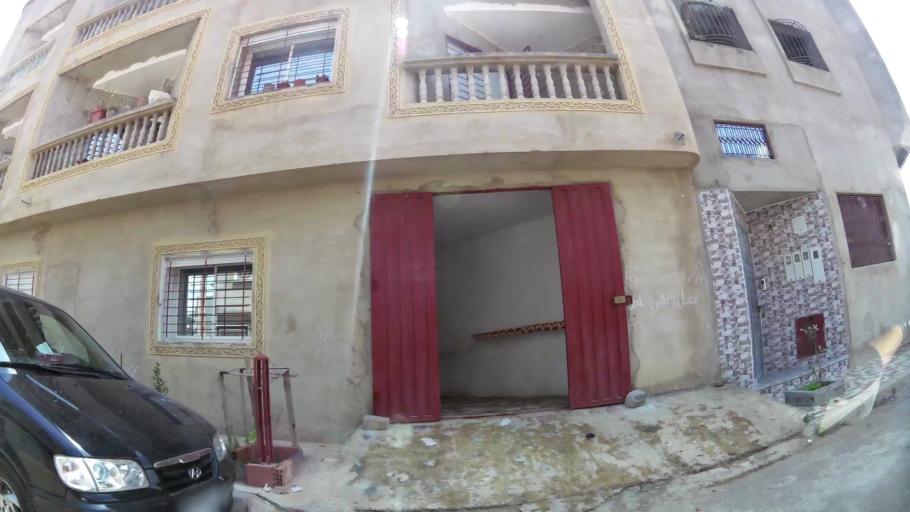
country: MA
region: Rabat-Sale-Zemmour-Zaer
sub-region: Khemisset
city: Tiflet
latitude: 34.0057
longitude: -6.5361
